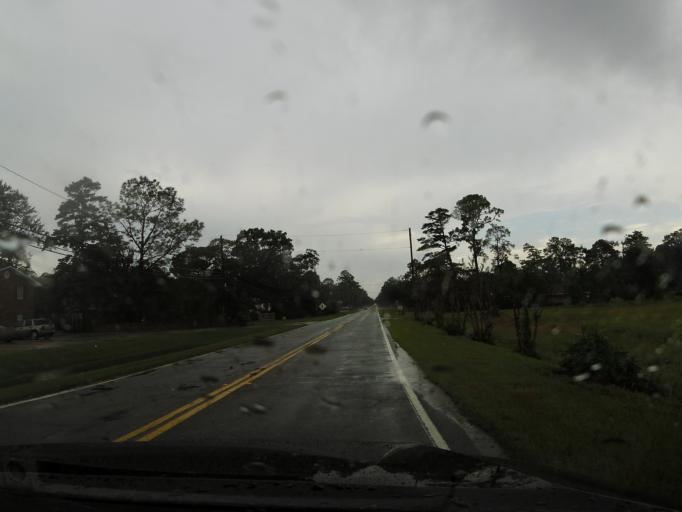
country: US
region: Georgia
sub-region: Wayne County
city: Jesup
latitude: 31.5965
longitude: -81.8724
